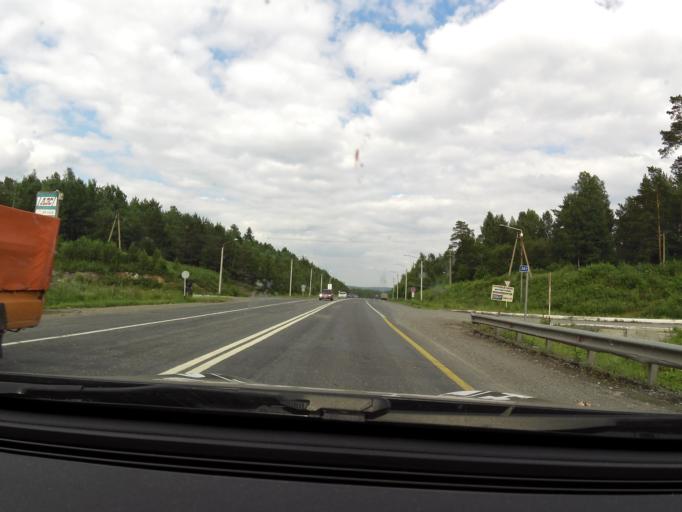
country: RU
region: Sverdlovsk
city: Druzhinino
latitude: 56.8056
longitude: 59.4845
